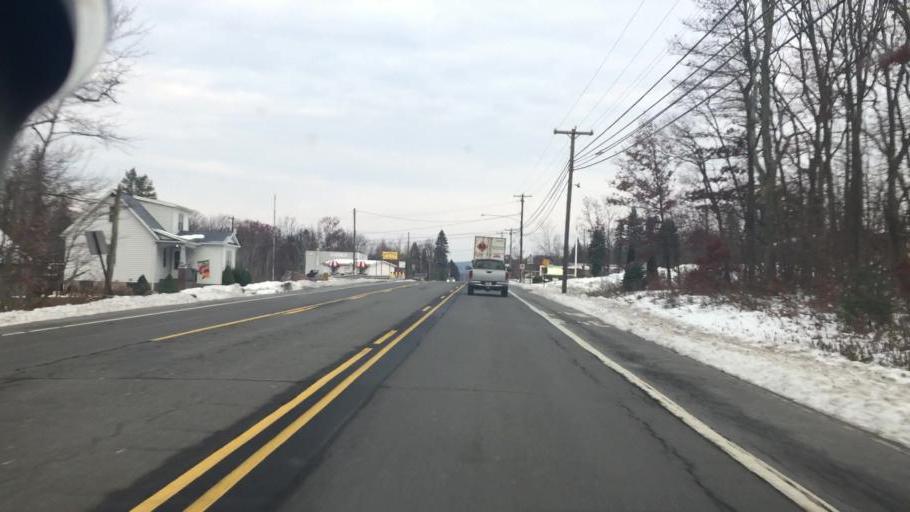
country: US
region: Pennsylvania
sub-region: Luzerne County
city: Mountain Top
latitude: 41.1338
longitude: -75.9041
